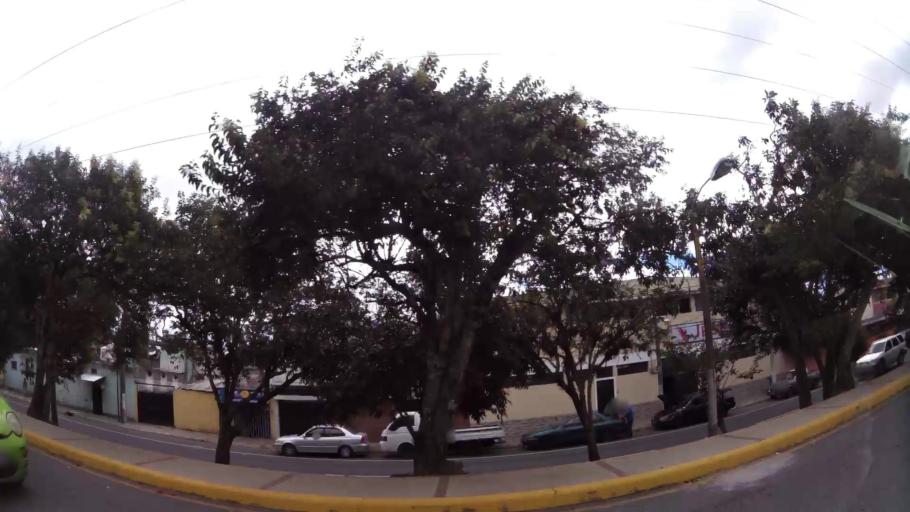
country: GT
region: Guatemala
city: Guatemala City
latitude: 14.6300
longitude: -90.5524
